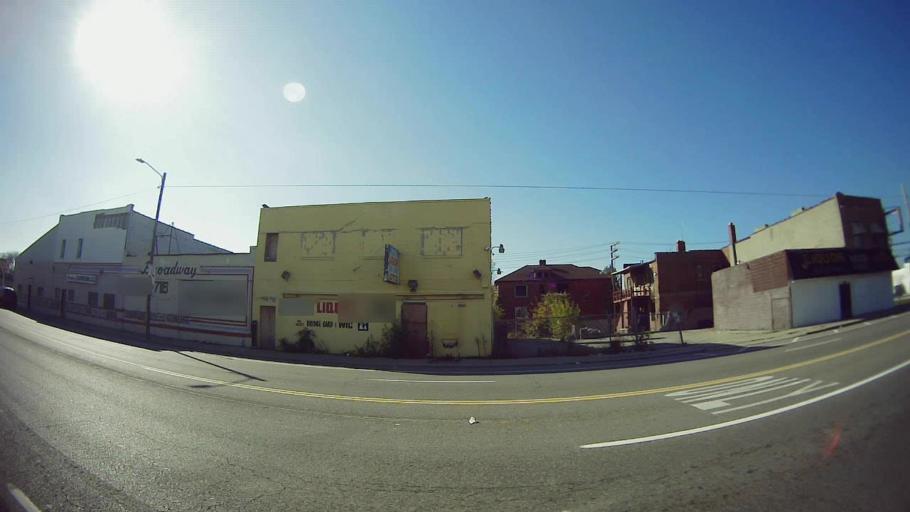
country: US
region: Michigan
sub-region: Wayne County
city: Highland Park
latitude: 42.3899
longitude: -83.1198
